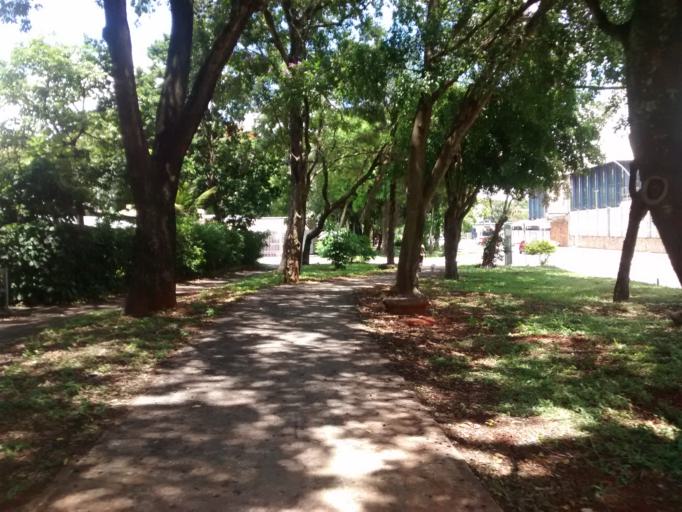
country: BR
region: Federal District
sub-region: Brasilia
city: Brasilia
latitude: -15.8168
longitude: -47.9167
